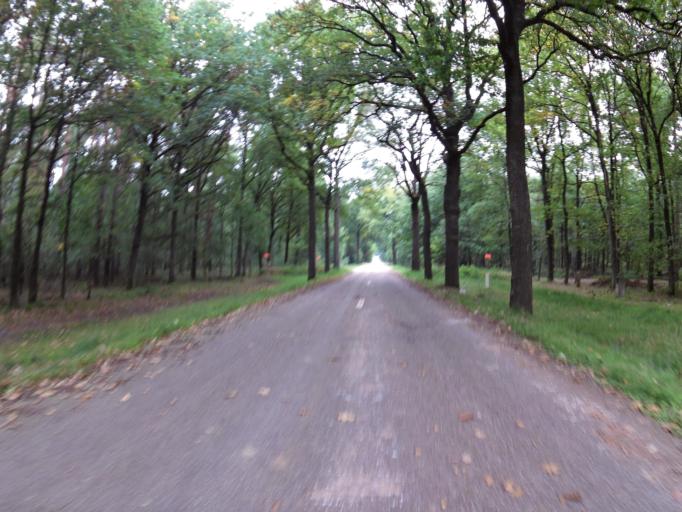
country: BE
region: Flanders
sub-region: Provincie Limburg
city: As
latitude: 50.9846
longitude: 5.5714
